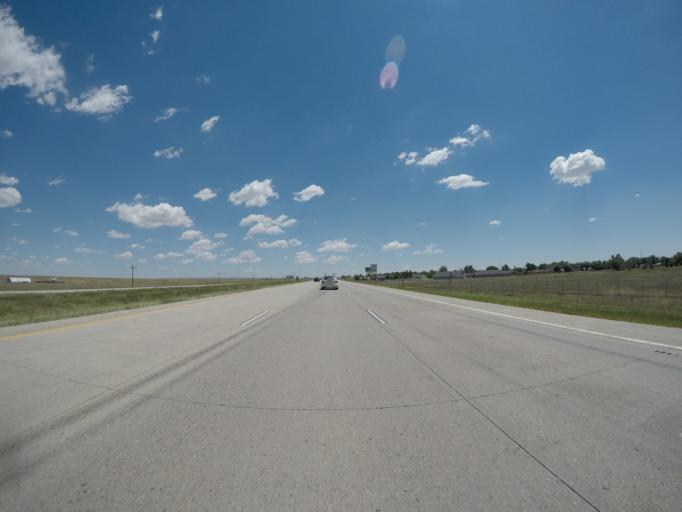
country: US
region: Colorado
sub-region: Lincoln County
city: Limon
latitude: 39.2733
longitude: -103.6962
